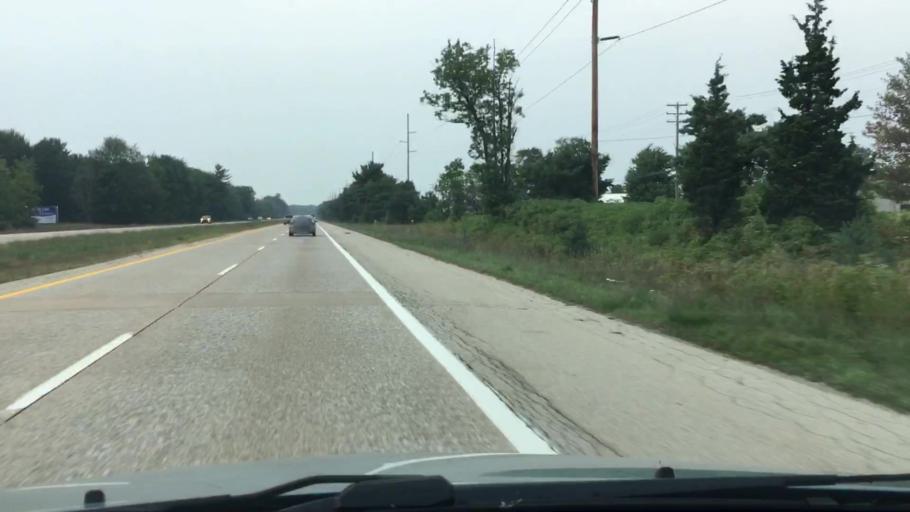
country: US
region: Michigan
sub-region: Ottawa County
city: Grand Haven
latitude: 43.0157
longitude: -86.2095
